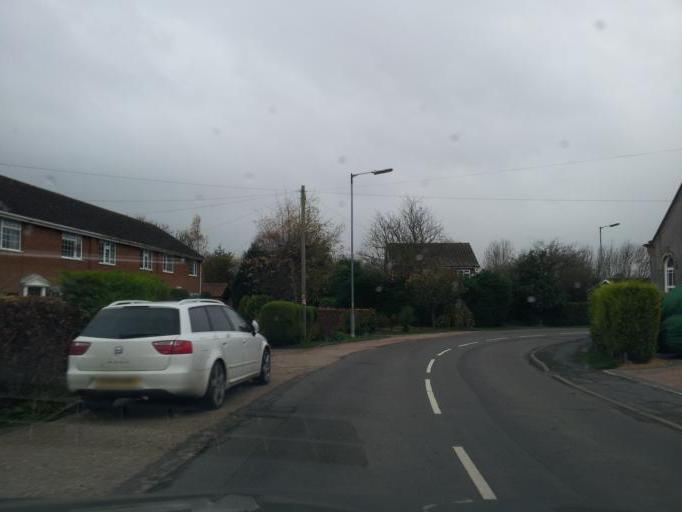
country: GB
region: England
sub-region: Lincolnshire
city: Louth
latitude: 53.3739
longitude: 0.0878
